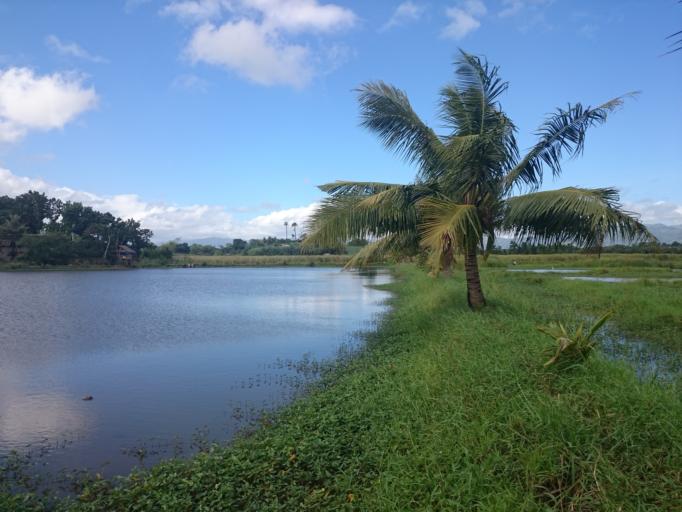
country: PH
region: Central Visayas
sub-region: Province of Negros Oriental
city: Tanjay
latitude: 9.5013
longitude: 123.1550
